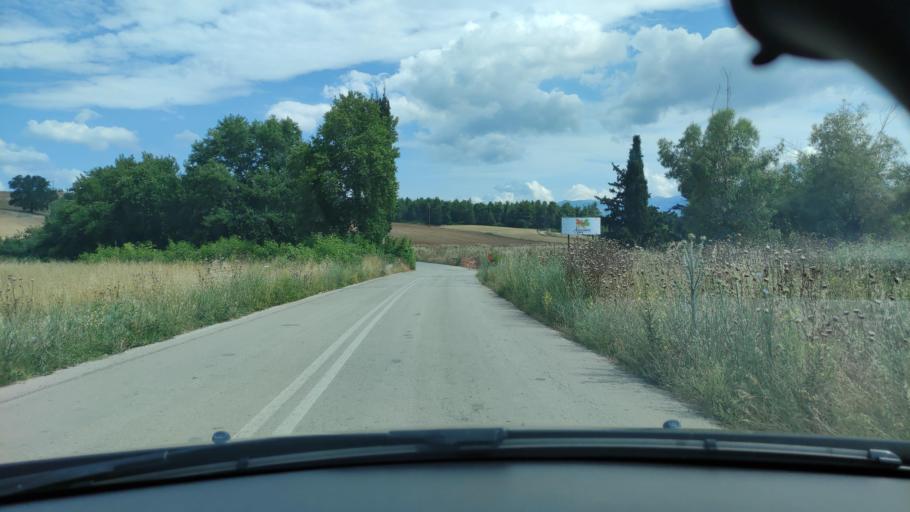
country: GR
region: Central Greece
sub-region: Nomos Evvoias
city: Afration
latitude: 38.5186
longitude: 23.7503
